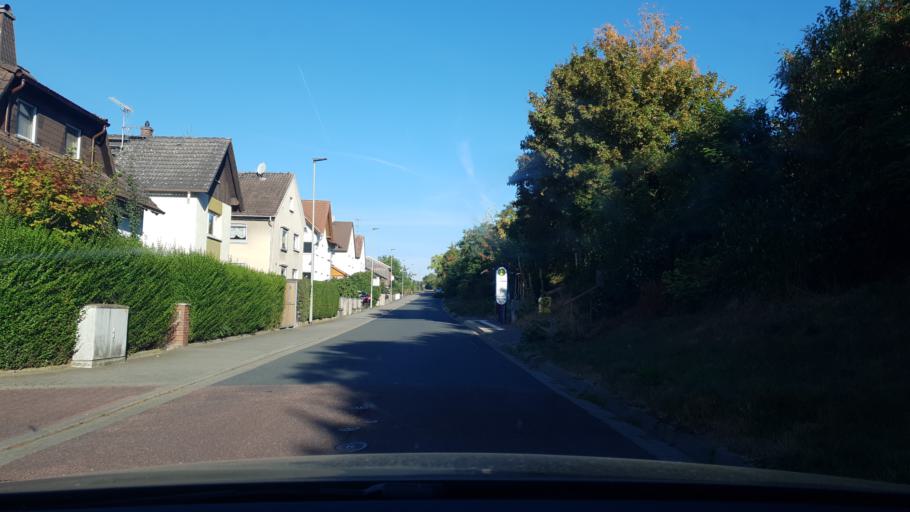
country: DE
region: Hesse
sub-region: Regierungsbezirk Darmstadt
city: Butzbach
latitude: 50.4553
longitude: 8.6545
